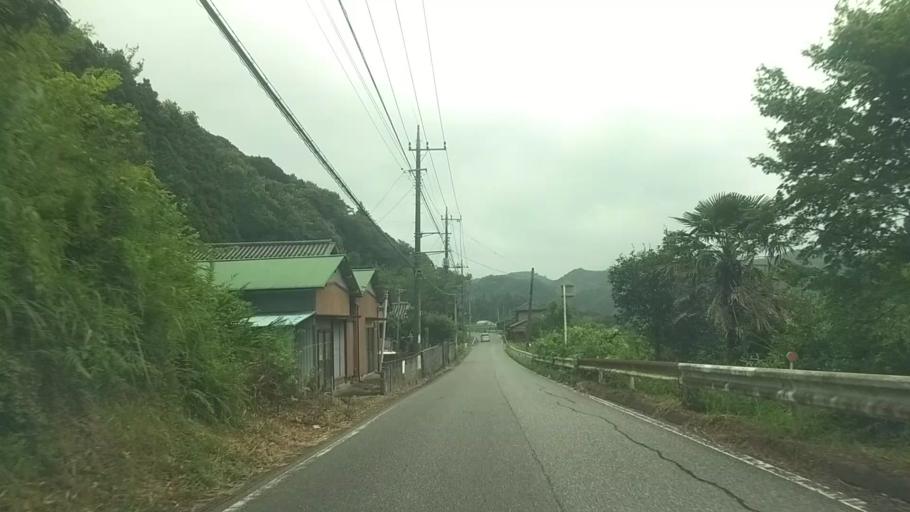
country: JP
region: Chiba
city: Kawaguchi
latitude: 35.2268
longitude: 140.0168
